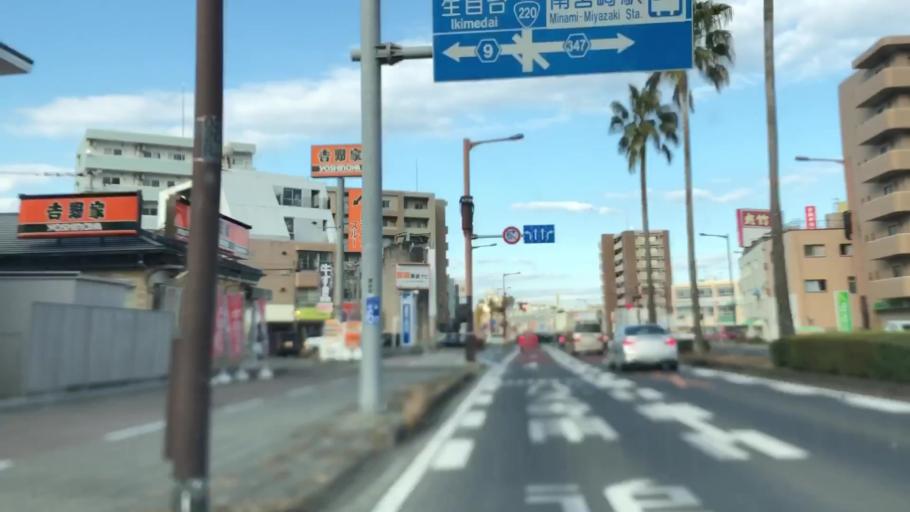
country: JP
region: Miyazaki
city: Miyazaki-shi
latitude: 31.8970
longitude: 131.4176
